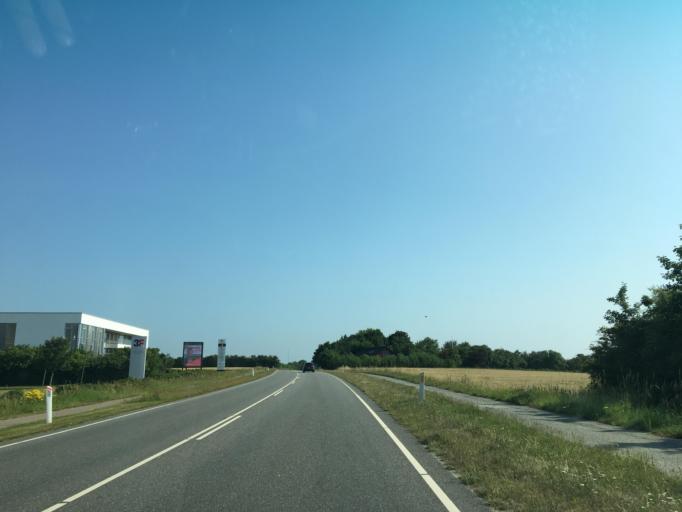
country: DK
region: North Denmark
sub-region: Thisted Kommune
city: Thisted
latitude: 56.9378
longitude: 8.6484
